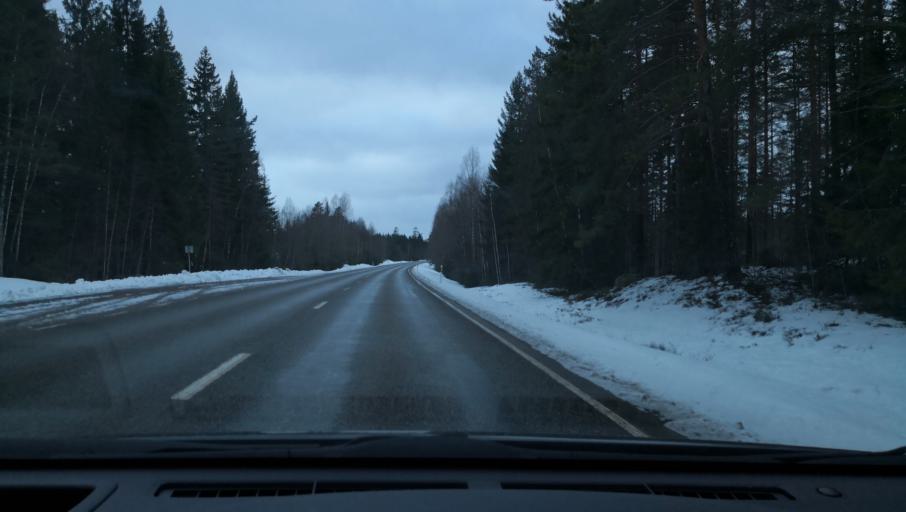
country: SE
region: Vaestmanland
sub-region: Surahammars Kommun
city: Ramnas
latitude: 59.7870
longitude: 15.9986
